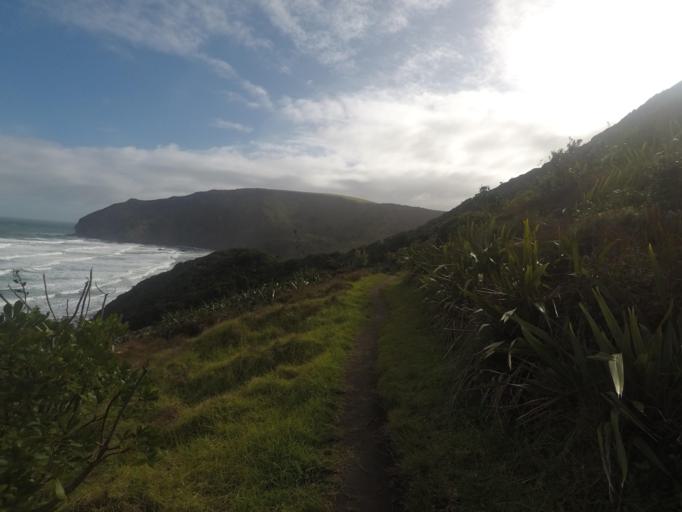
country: NZ
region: Auckland
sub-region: Auckland
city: Muriwai Beach
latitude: -36.8868
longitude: 174.4399
